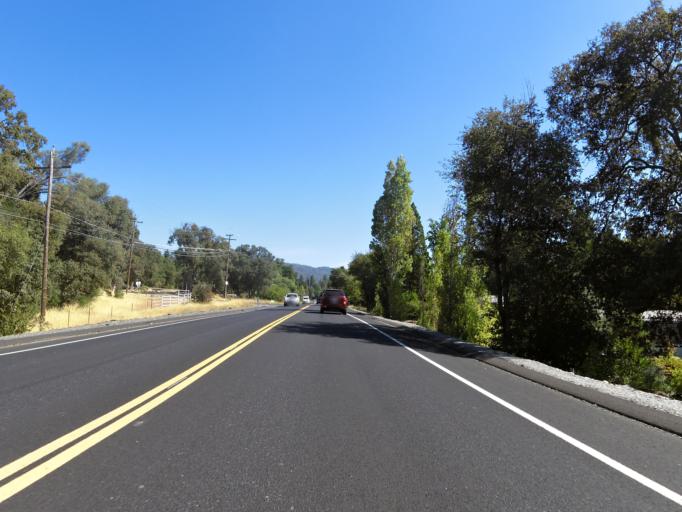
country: US
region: California
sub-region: Calaveras County
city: Murphys
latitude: 38.1112
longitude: -120.4584
